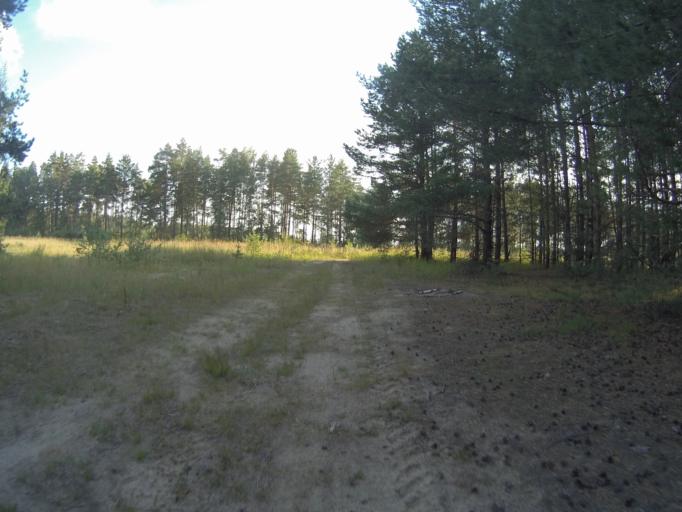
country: RU
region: Vladimir
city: Kommunar
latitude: 56.0599
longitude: 40.4412
